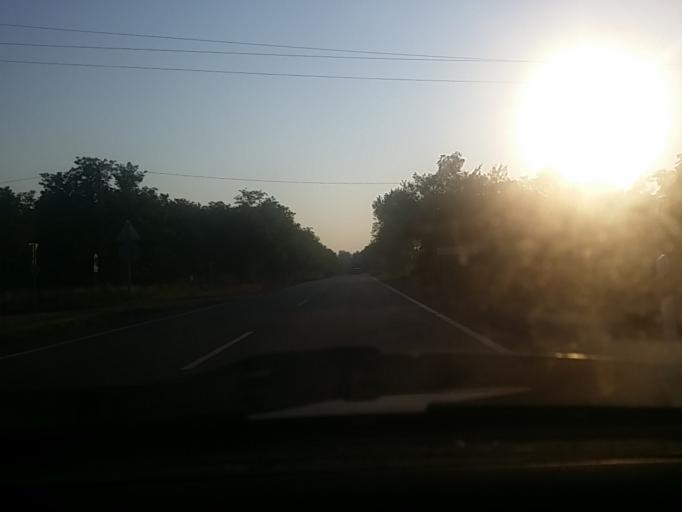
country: HU
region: Jasz-Nagykun-Szolnok
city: Jaszbereny
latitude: 47.4734
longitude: 19.8636
